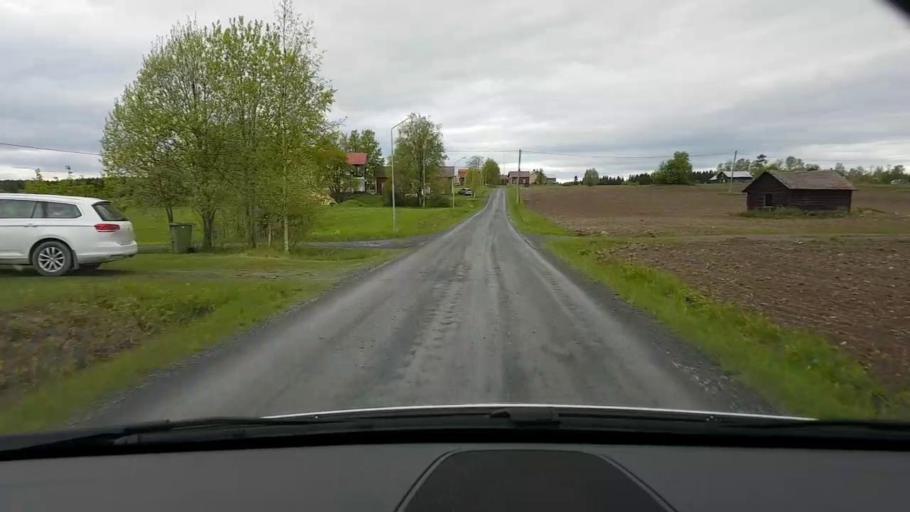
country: SE
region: Jaemtland
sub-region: Krokoms Kommun
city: Valla
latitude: 63.3042
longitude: 14.0164
